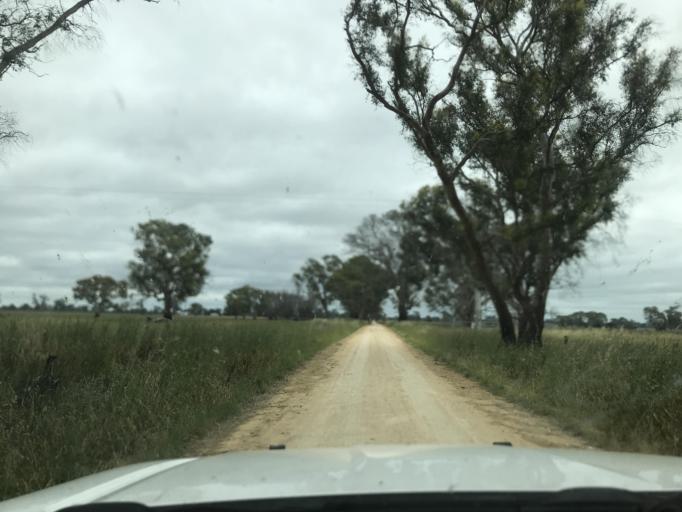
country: AU
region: South Australia
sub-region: Wattle Range
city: Penola
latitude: -37.1817
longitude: 141.0856
